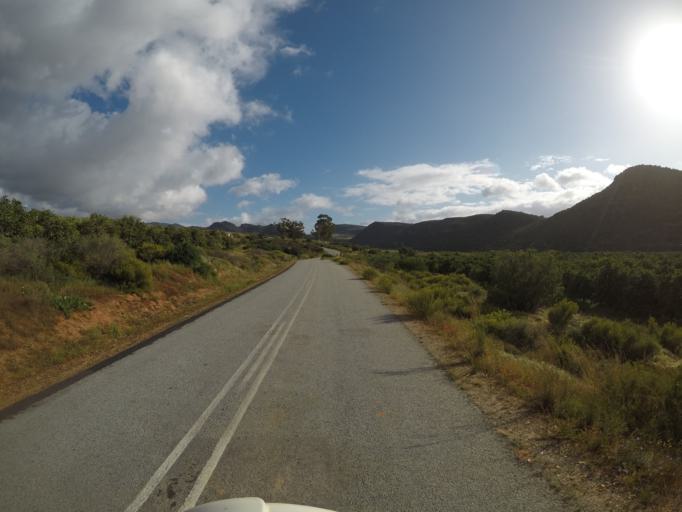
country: ZA
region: Western Cape
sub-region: West Coast District Municipality
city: Clanwilliam
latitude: -32.4345
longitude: 18.9394
